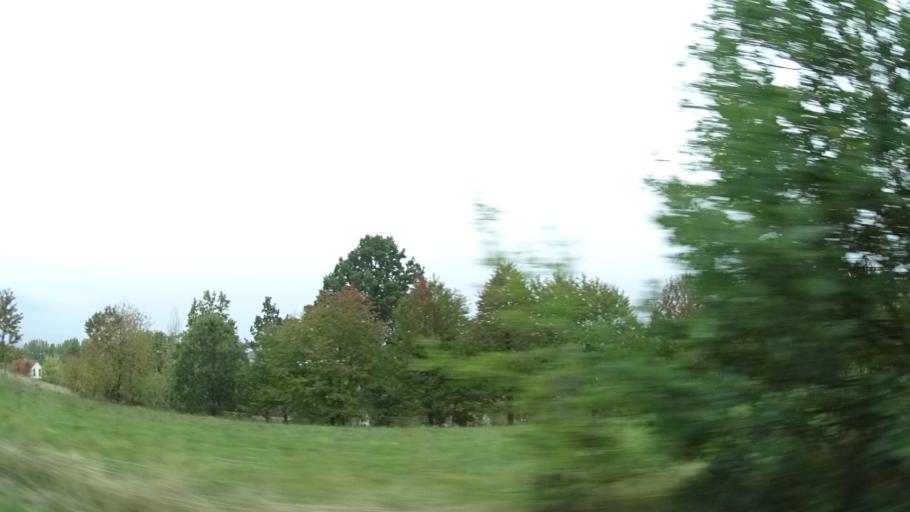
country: DE
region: Hesse
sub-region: Regierungsbezirk Kassel
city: Eichenzell
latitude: 50.4733
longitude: 9.7195
